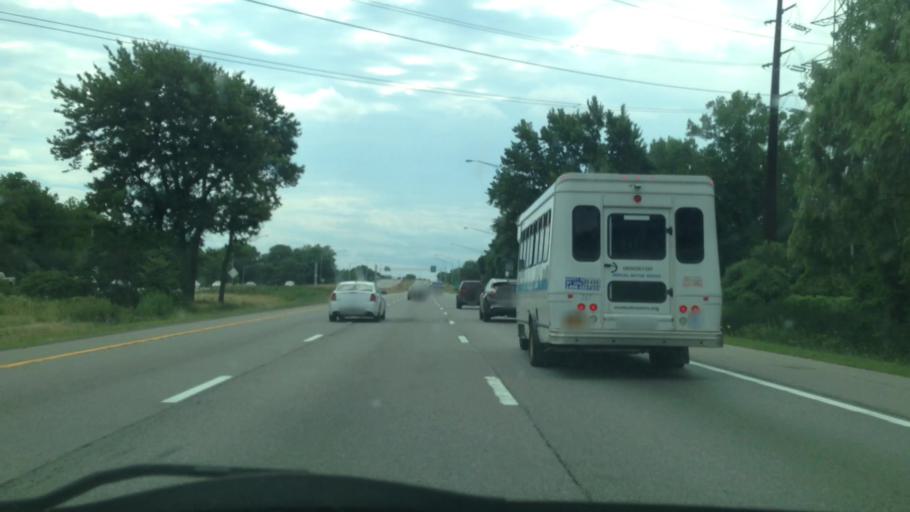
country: US
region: New York
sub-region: Monroe County
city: North Gates
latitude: 43.1440
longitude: -77.6736
